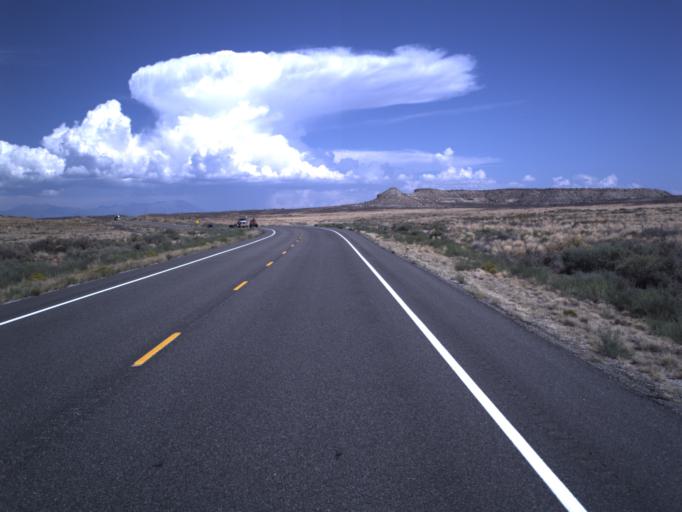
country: US
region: Utah
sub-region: San Juan County
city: Blanding
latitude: 37.3301
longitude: -109.5202
